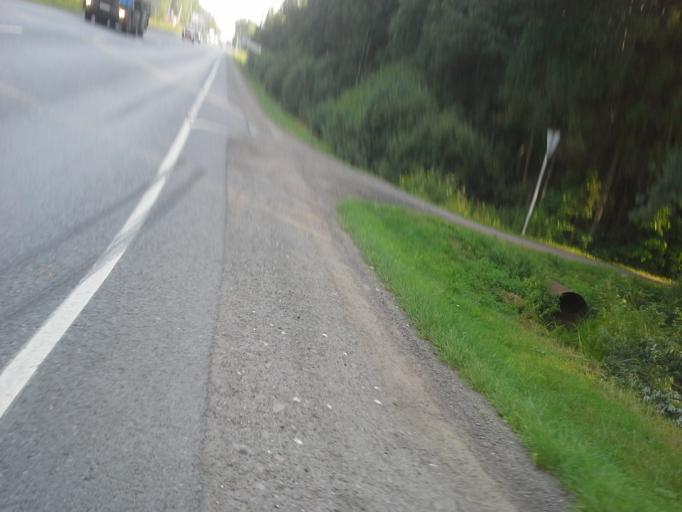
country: RU
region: Moskovskaya
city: Istra
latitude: 55.9099
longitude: 36.9453
